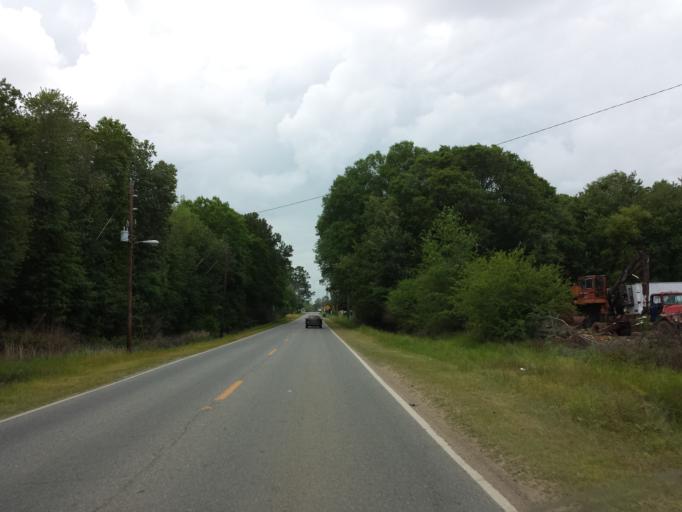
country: US
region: Georgia
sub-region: Cook County
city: Sparks
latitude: 31.2661
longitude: -83.4637
